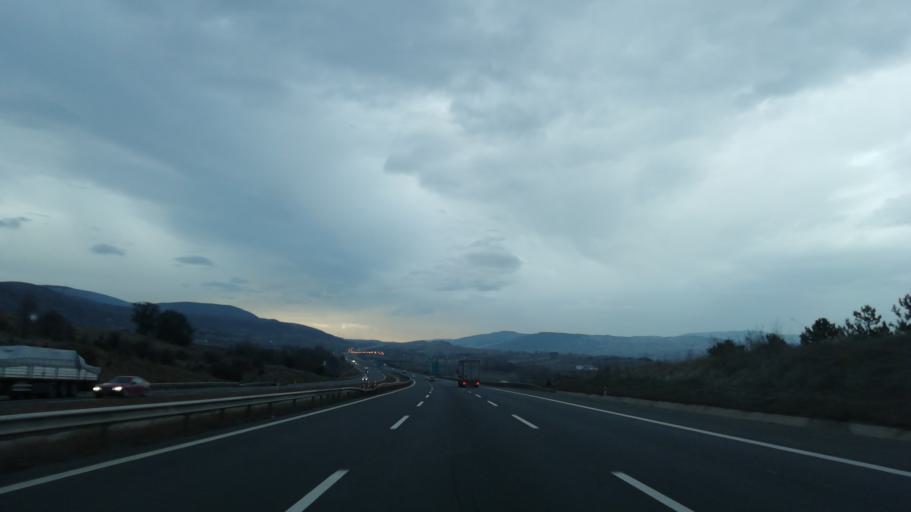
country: TR
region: Bolu
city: Yenicaga
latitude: 40.7658
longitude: 32.0269
